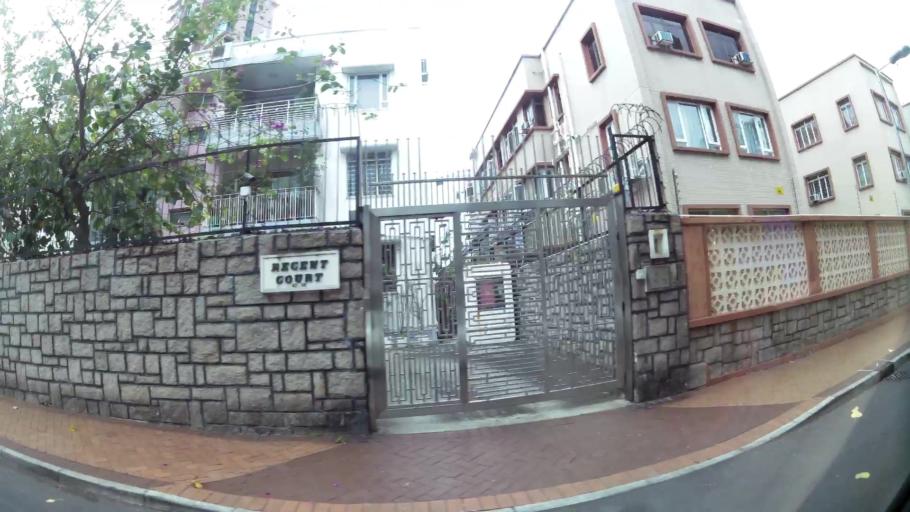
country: HK
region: Sham Shui Po
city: Sham Shui Po
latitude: 22.3321
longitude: 114.1736
